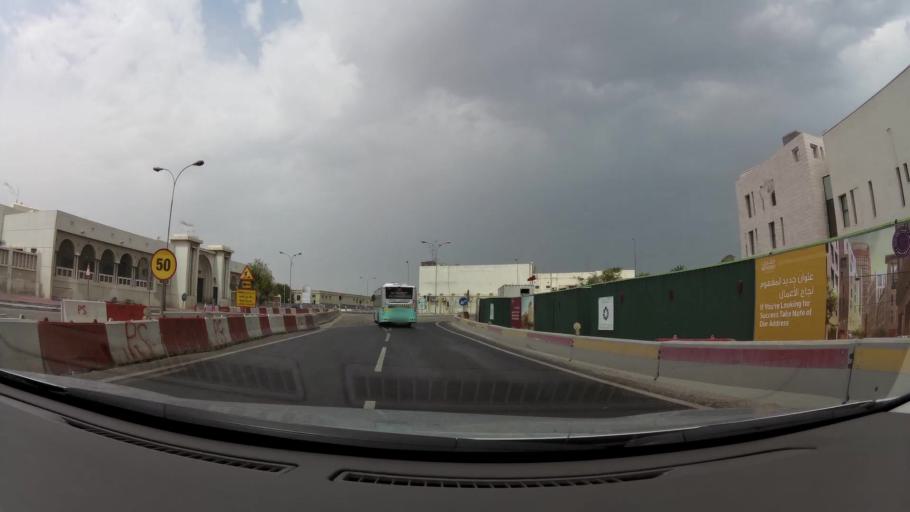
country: QA
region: Baladiyat ad Dawhah
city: Doha
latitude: 25.2879
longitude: 51.5237
